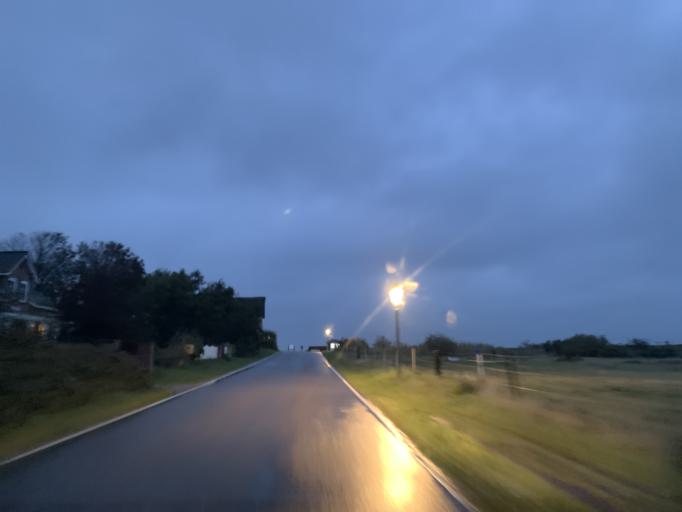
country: DE
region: Schleswig-Holstein
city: Wittdun
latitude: 54.6389
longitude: 8.3785
